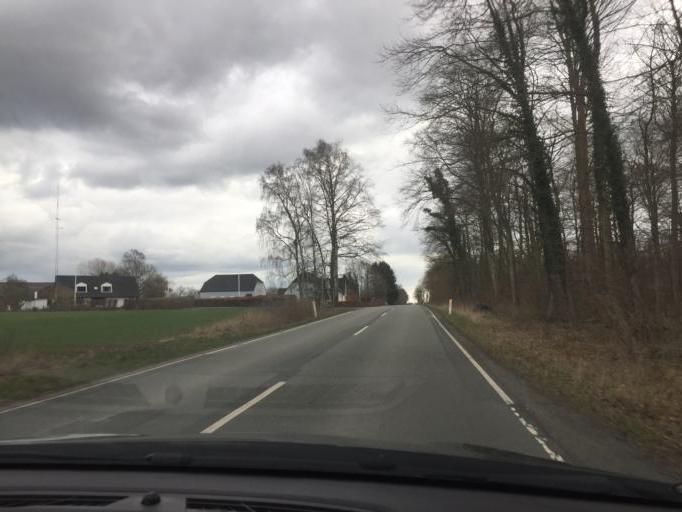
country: DK
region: South Denmark
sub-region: Kerteminde Kommune
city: Langeskov
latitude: 55.3030
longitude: 10.5932
